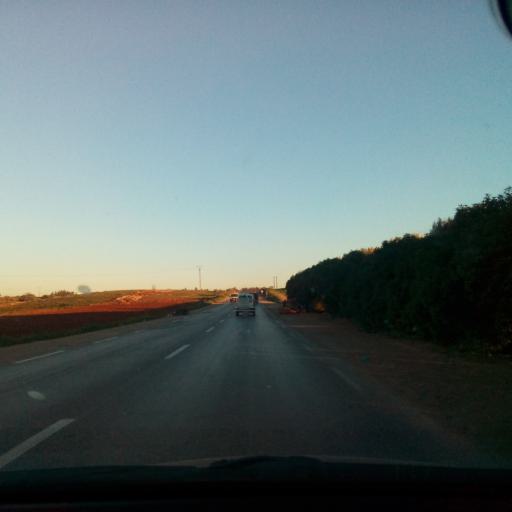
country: DZ
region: Relizane
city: Relizane
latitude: 35.7359
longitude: 0.2970
